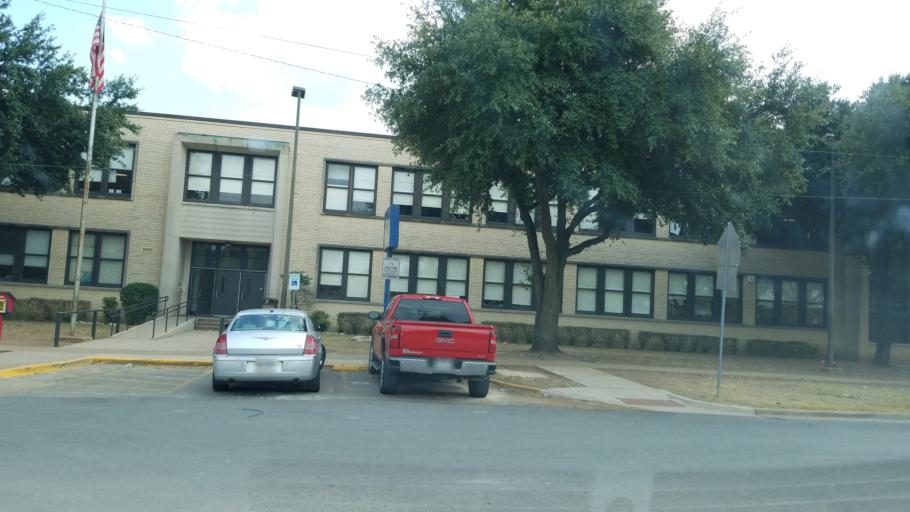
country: US
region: Texas
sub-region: Dallas County
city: Dallas
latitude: 32.7695
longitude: -96.8437
